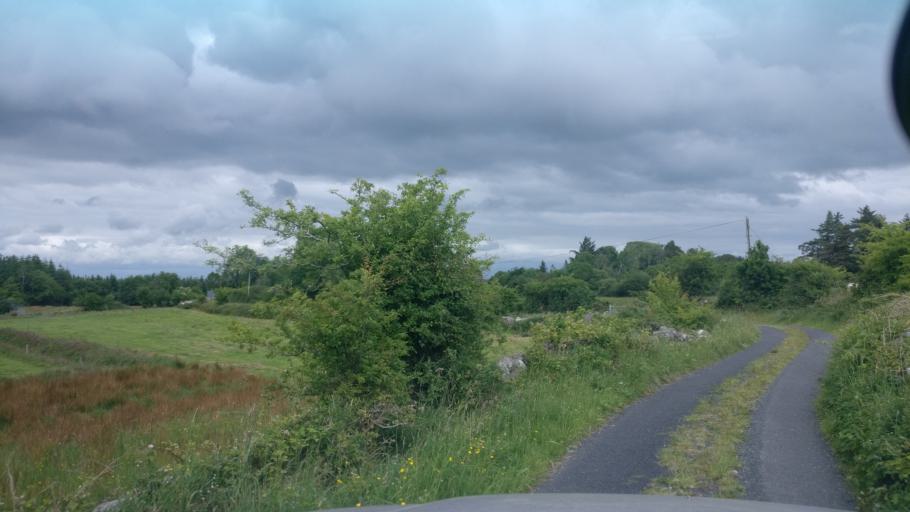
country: IE
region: Connaught
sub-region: County Galway
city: Loughrea
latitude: 53.1527
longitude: -8.5759
